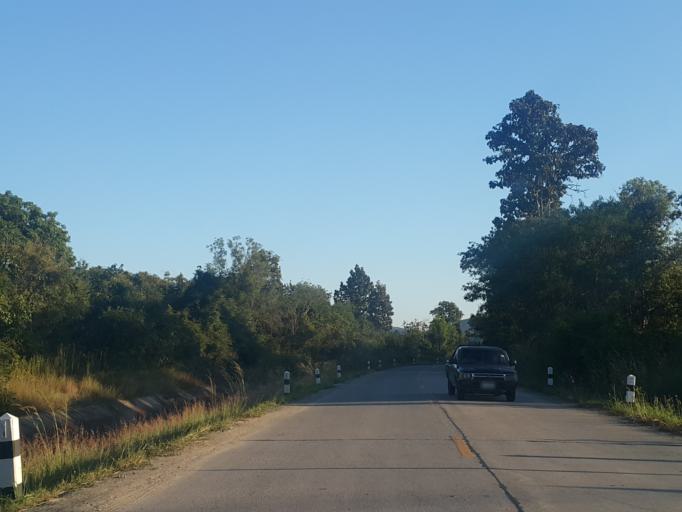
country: TH
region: Chiang Mai
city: San Sai
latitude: 18.8802
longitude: 99.1584
